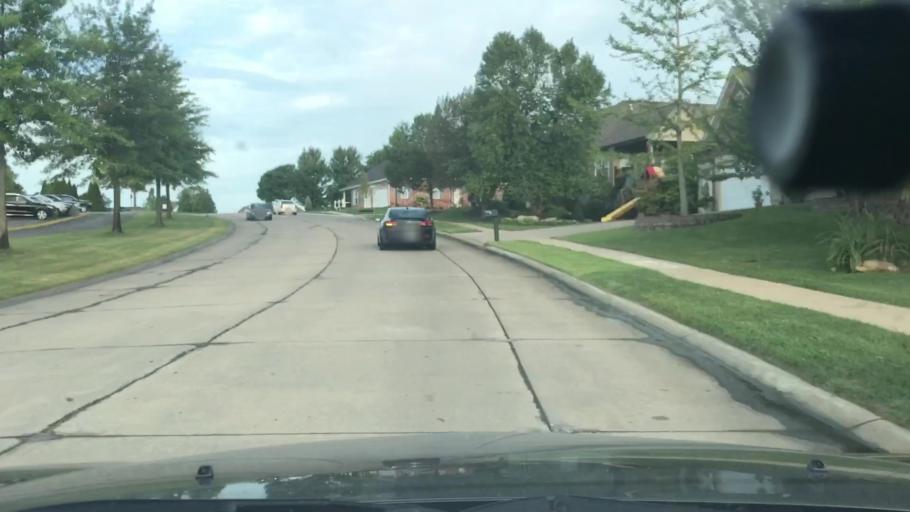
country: US
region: Missouri
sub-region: Saint Charles County
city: Wentzville
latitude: 38.8187
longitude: -90.8955
